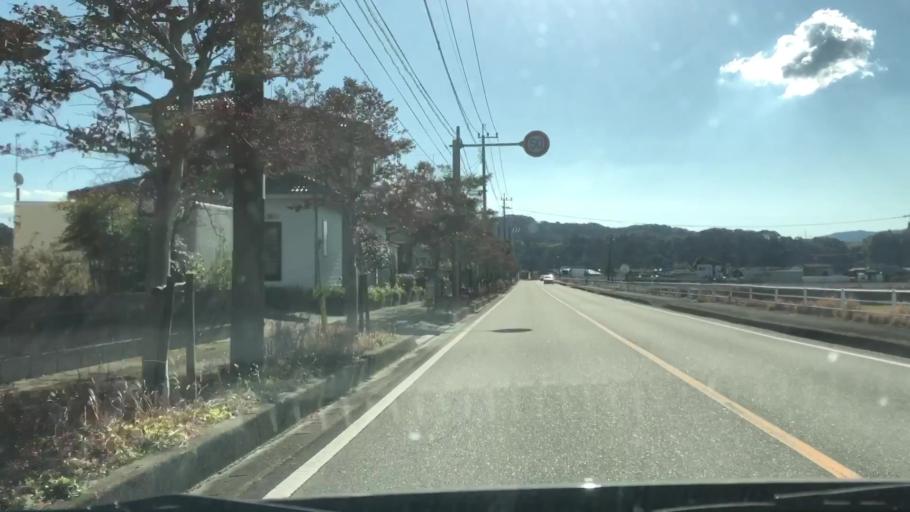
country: JP
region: Kagoshima
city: Satsumasendai
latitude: 31.8592
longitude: 130.3923
